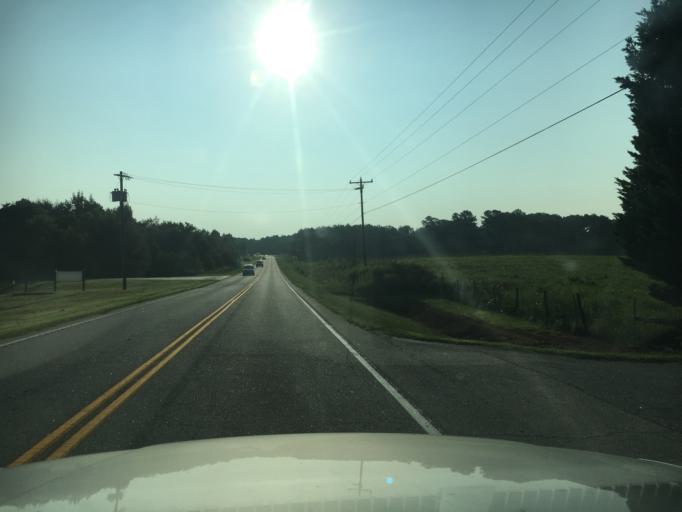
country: US
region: South Carolina
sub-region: Spartanburg County
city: Inman
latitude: 35.0845
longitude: -82.0540
